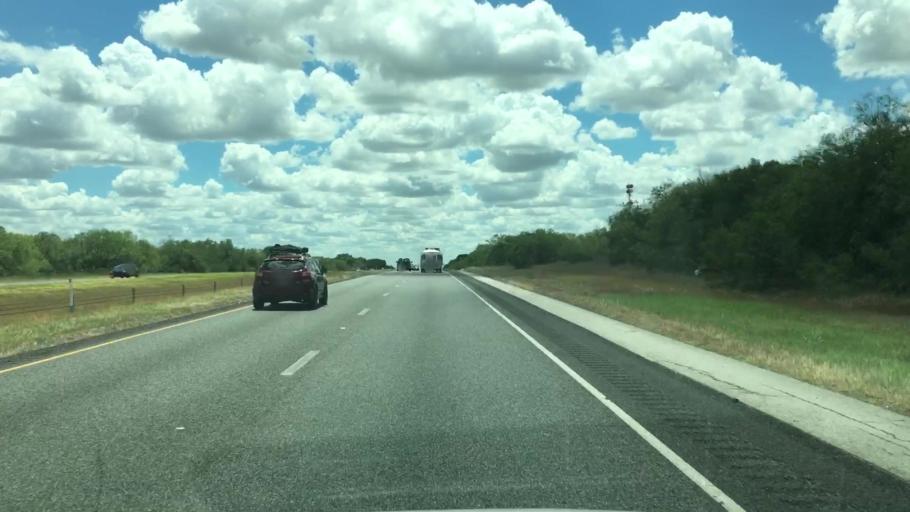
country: US
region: Texas
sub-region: Bexar County
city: Elmendorf
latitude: 29.1339
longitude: -98.4300
